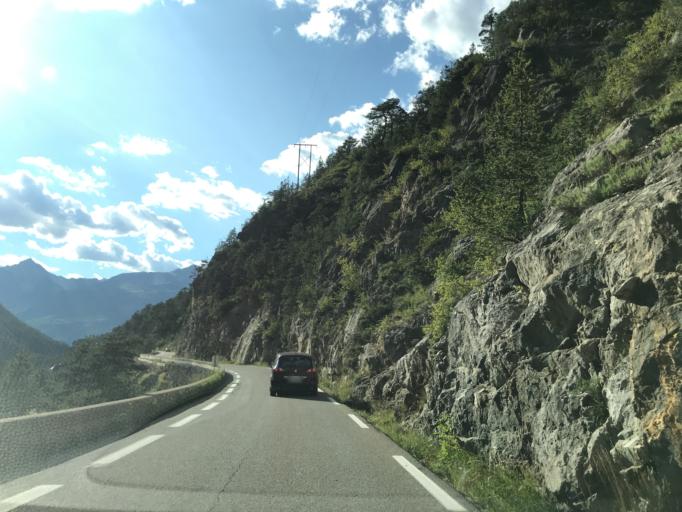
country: FR
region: Provence-Alpes-Cote d'Azur
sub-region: Departement des Hautes-Alpes
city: Briancon
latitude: 44.8785
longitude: 6.6799
